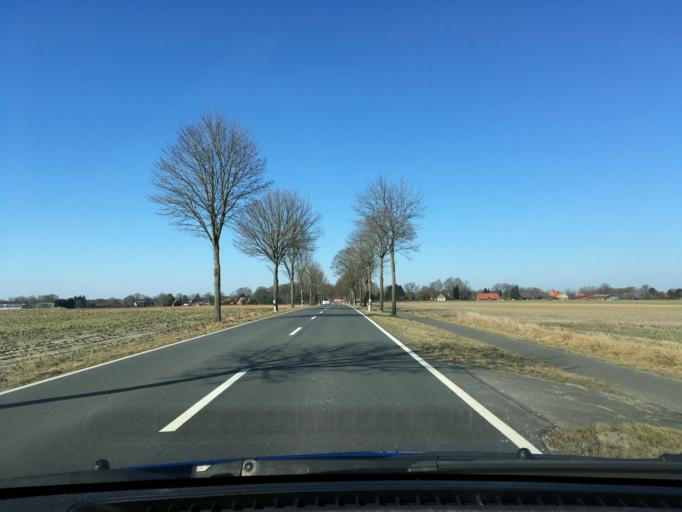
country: DE
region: Lower Saxony
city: Hemslingen
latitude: 53.0754
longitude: 9.6272
